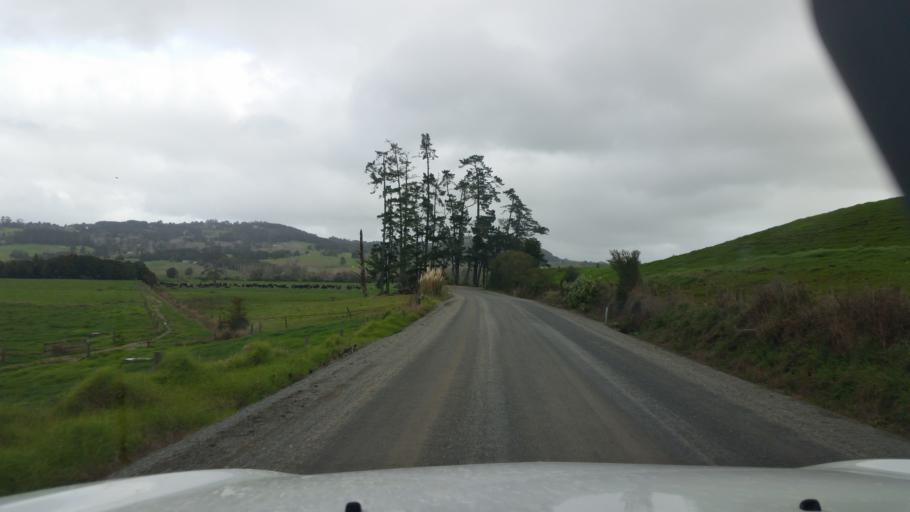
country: NZ
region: Northland
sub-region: Whangarei
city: Maungatapere
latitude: -35.6205
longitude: 174.1979
